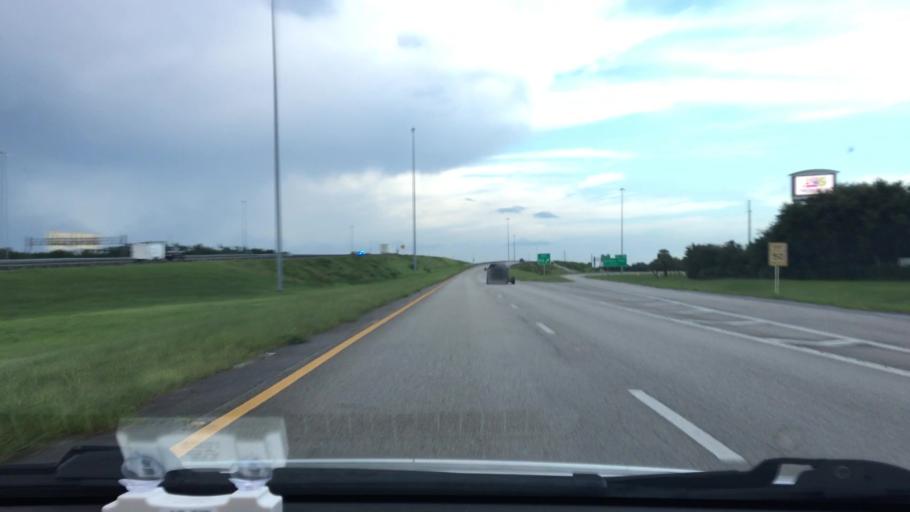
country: US
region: Florida
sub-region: Seminole County
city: Heathrow
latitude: 28.7928
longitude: -81.3465
